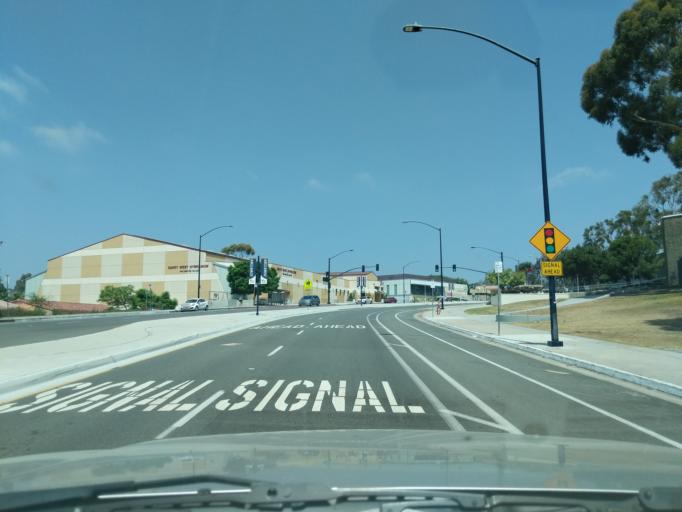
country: US
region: California
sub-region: San Diego County
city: San Diego
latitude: 32.7197
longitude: -117.1538
